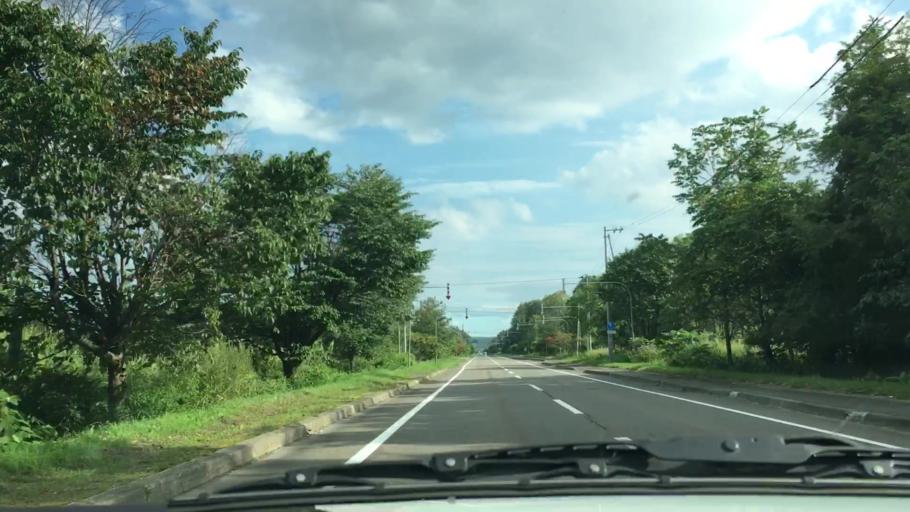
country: JP
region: Hokkaido
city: Otofuke
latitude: 43.3234
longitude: 143.3005
